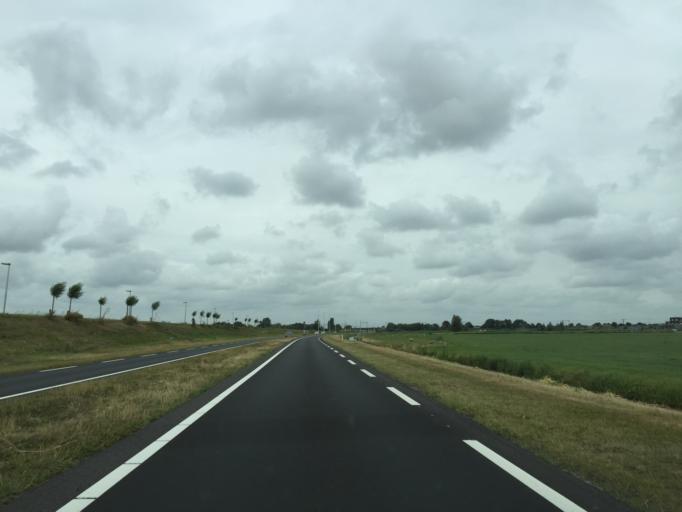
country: NL
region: South Holland
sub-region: Gemeente Lansingerland
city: Berkel en Rodenrijs
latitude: 51.9868
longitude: 4.4483
